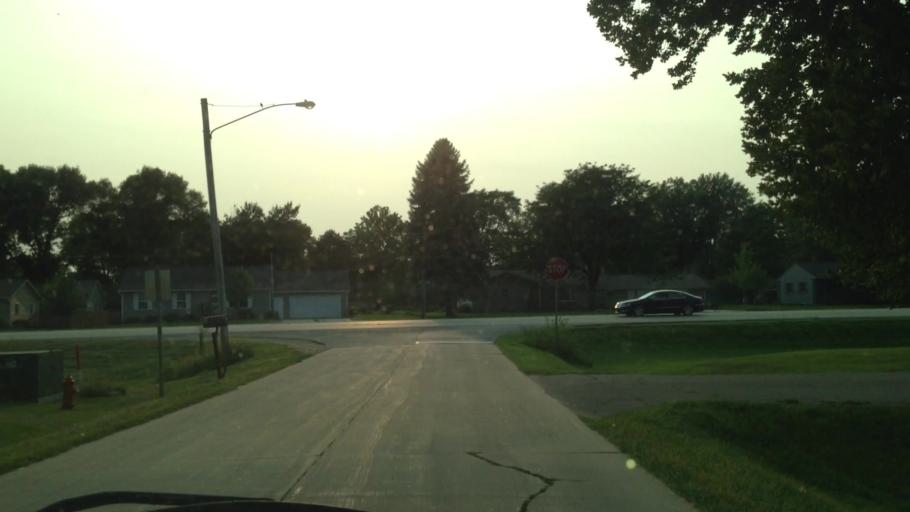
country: US
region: Iowa
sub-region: Benton County
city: Walford
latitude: 41.7992
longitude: -91.8745
